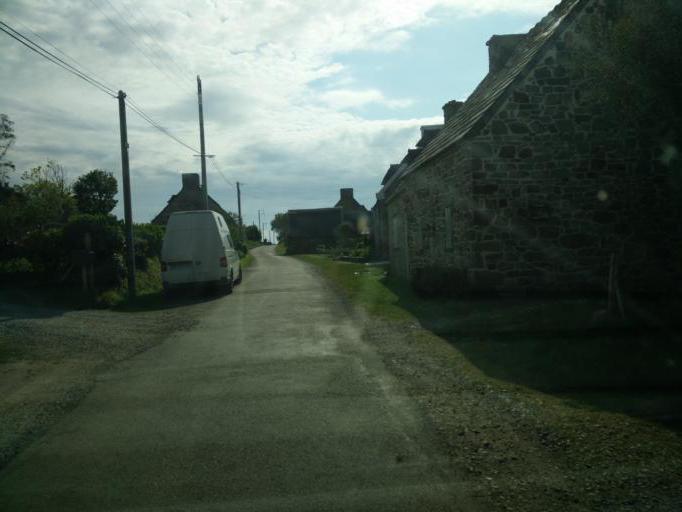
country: FR
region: Brittany
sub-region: Departement du Finistere
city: Crozon
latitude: 48.2346
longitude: -4.5492
